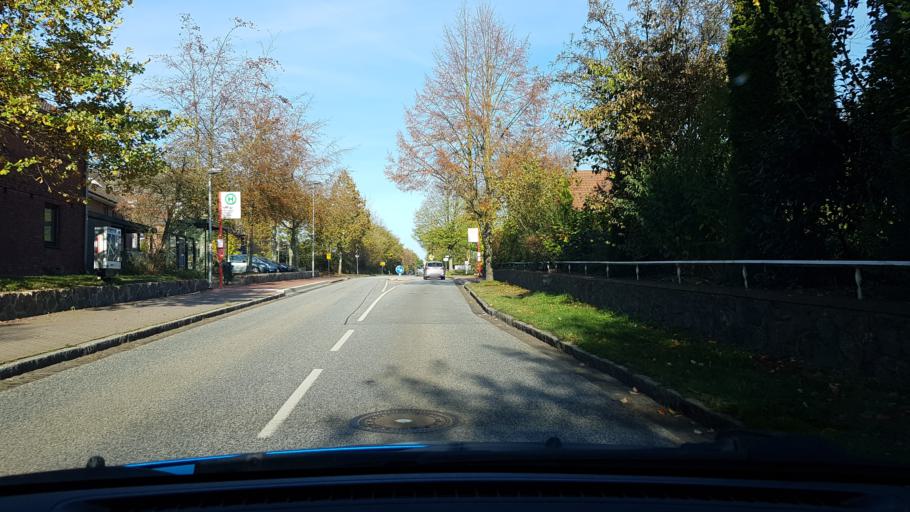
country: DE
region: Schleswig-Holstein
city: Escheburg
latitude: 53.4663
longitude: 10.3091
